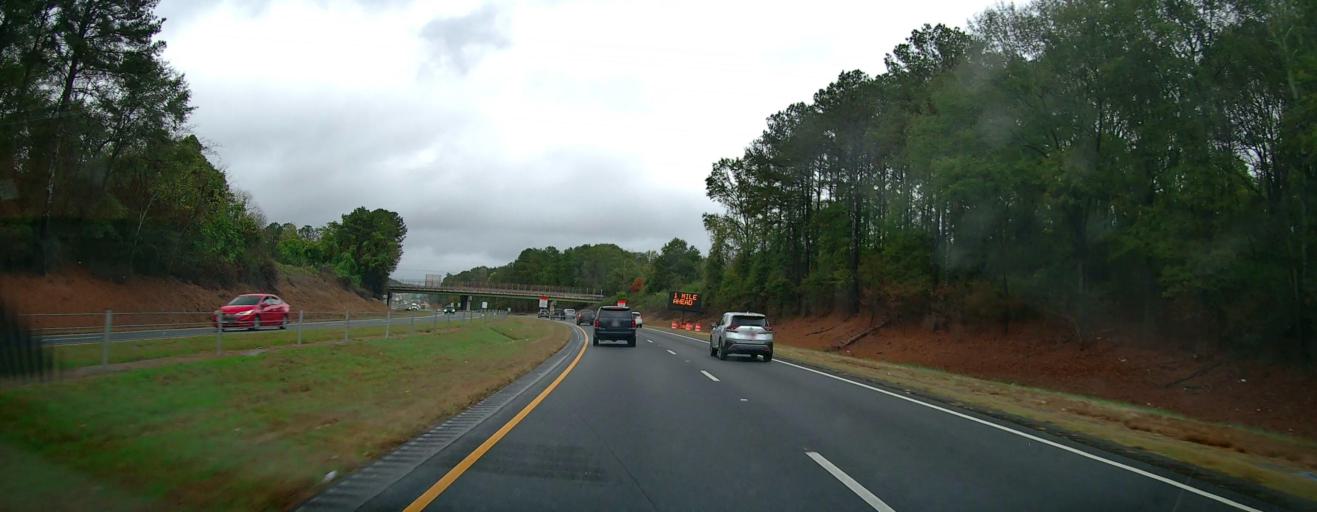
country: US
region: Georgia
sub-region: Clarke County
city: Athens
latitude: 33.9532
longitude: -83.3497
